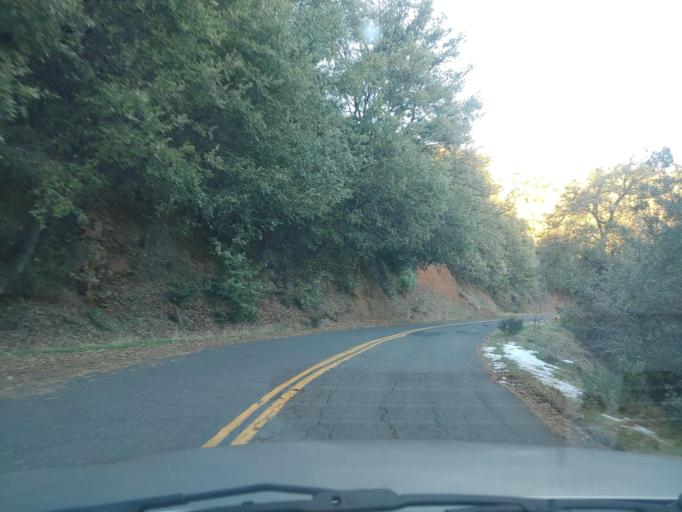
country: US
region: California
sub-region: Tuolumne County
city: Cedar Ridge
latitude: 38.0430
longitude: -120.3301
